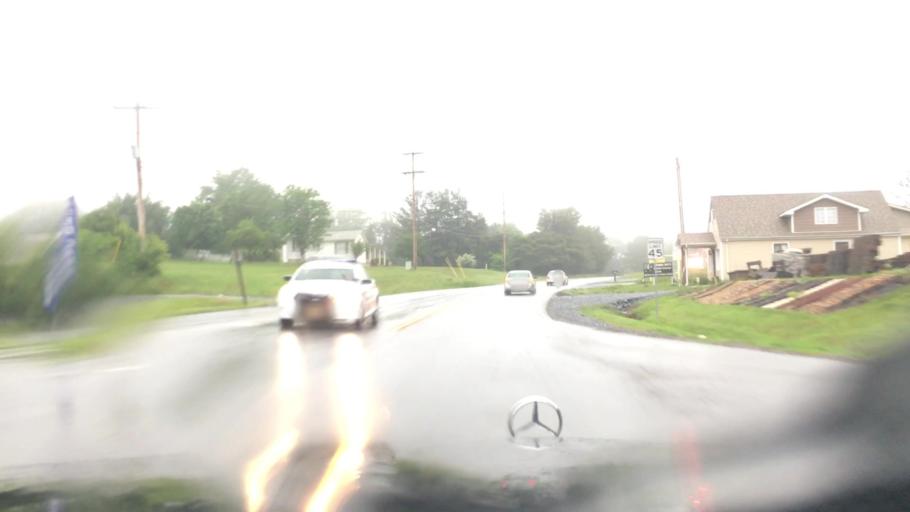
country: US
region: Virginia
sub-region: Campbell County
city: Timberlake
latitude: 37.3227
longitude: -79.2317
